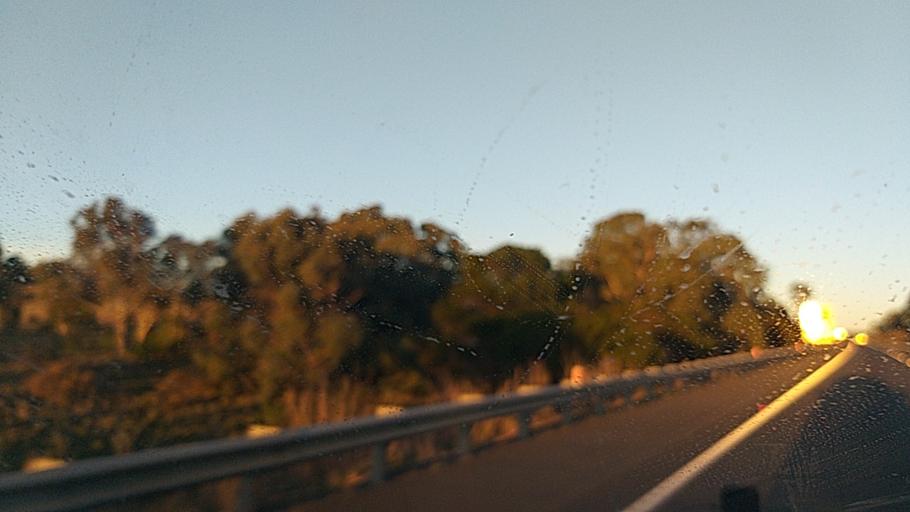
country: AU
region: New South Wales
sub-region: Goulburn Mulwaree
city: Goulburn
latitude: -34.7373
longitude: 149.7857
